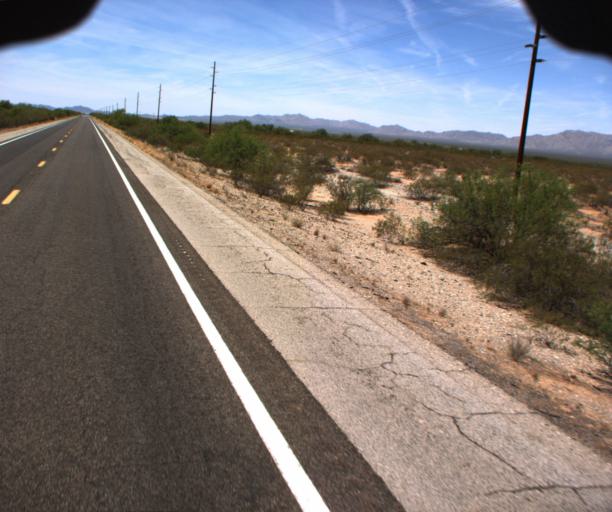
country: US
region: Arizona
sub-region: La Paz County
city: Salome
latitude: 33.8545
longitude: -113.4387
